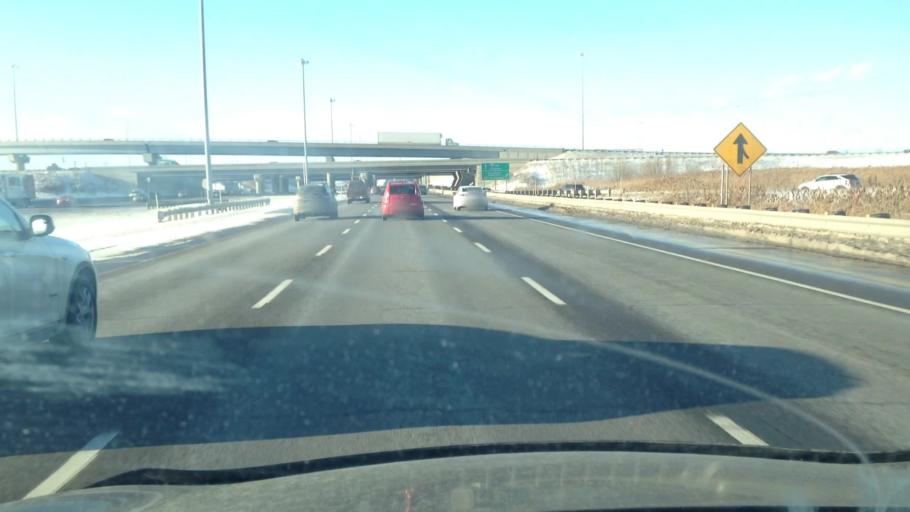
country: CA
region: Quebec
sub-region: Laurentides
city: Boisbriand
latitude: 45.6256
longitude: -73.8375
